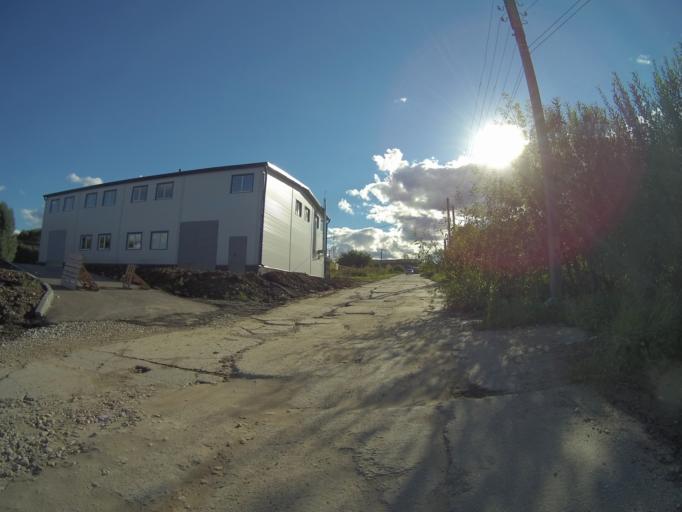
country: RU
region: Vladimir
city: Vladimir
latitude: 56.1787
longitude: 40.3616
